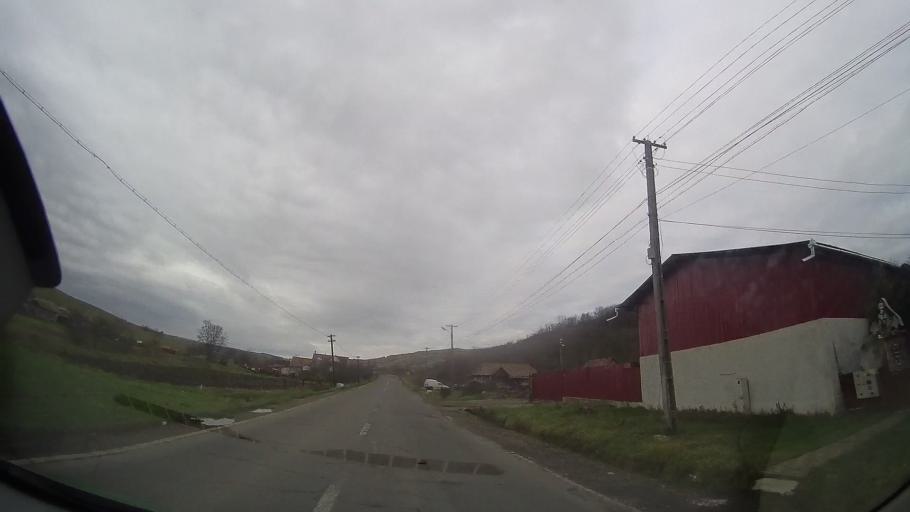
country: RO
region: Mures
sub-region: Comuna Craesti
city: Craiesti
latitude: 46.7584
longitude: 24.4082
